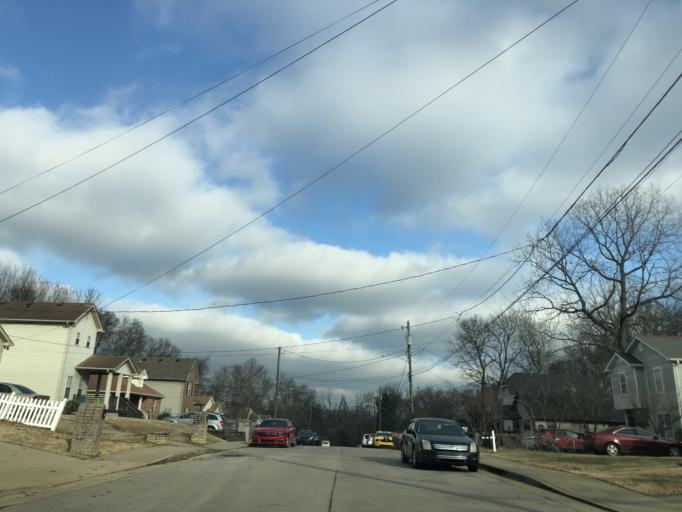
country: US
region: Tennessee
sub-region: Davidson County
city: Nashville
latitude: 36.2038
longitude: -86.7855
